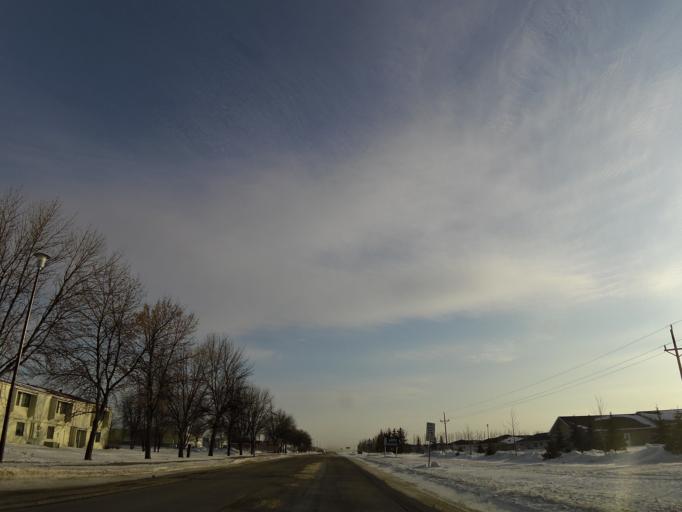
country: US
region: North Dakota
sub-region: Walsh County
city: Grafton
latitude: 48.4092
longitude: -97.4267
